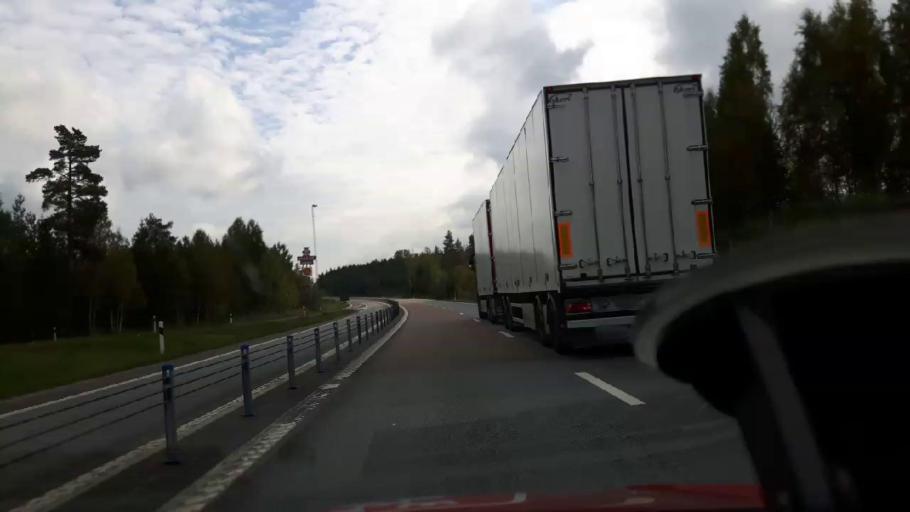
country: SE
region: Gaevleborg
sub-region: Gavle Kommun
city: Norrsundet
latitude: 60.9010
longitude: 17.0187
